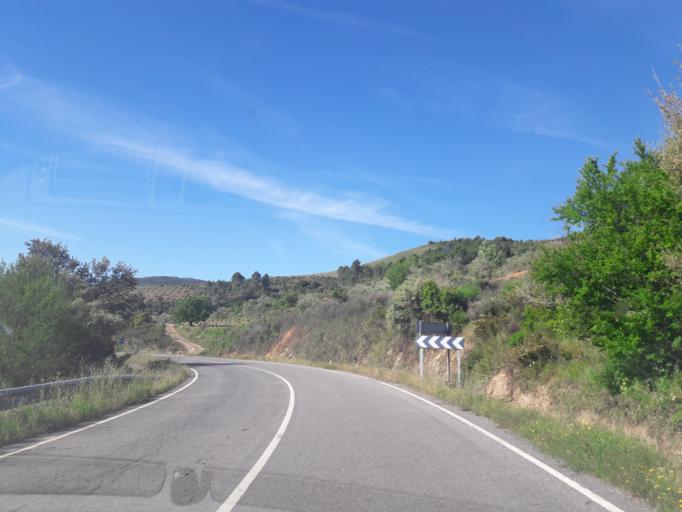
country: ES
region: Castille and Leon
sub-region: Provincia de Salamanca
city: Sotoserrano
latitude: 40.4254
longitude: -6.0380
